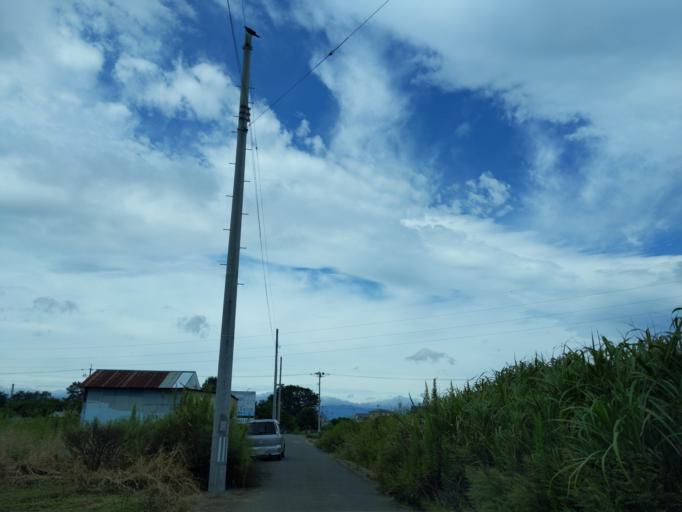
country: JP
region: Fukushima
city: Koriyama
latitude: 37.3996
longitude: 140.4057
